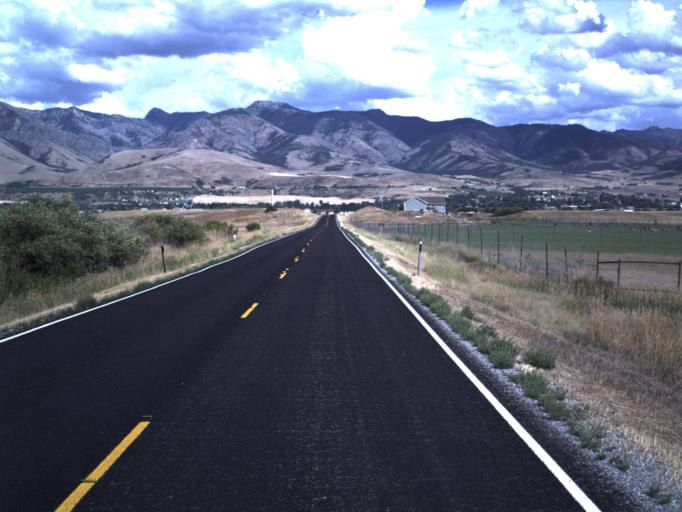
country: US
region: Utah
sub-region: Cache County
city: Richmond
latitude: 41.9243
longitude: -111.8471
